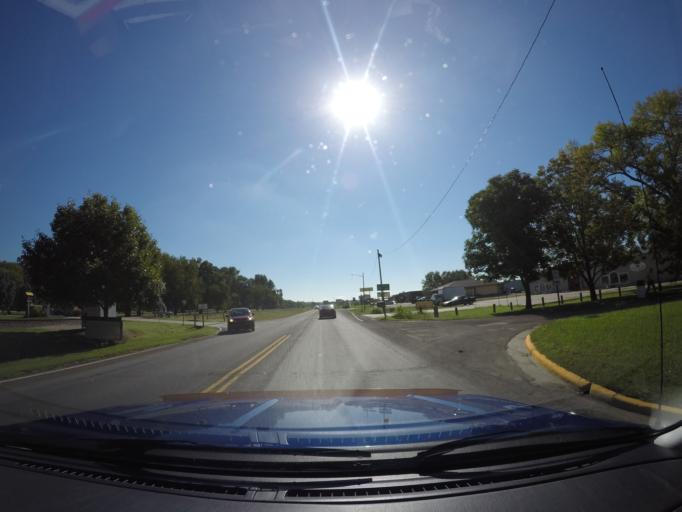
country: US
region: Kansas
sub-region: Pottawatomie County
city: Saint Marys
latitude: 39.1905
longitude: -96.0604
